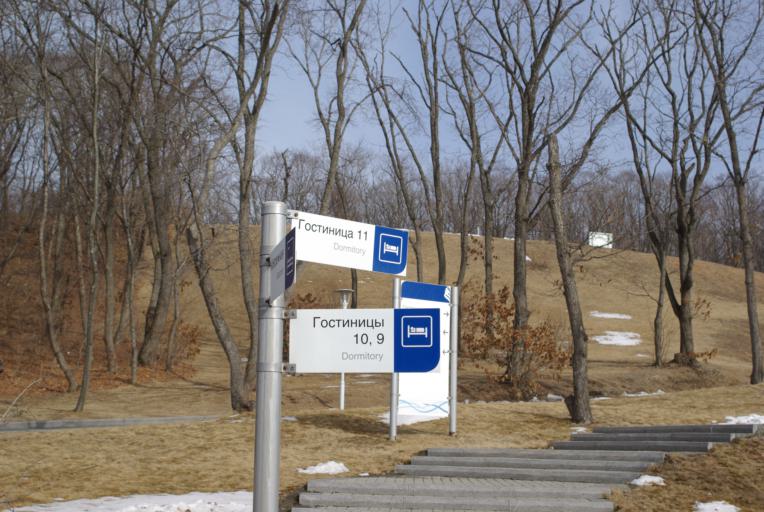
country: RU
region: Primorskiy
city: Russkiy
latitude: 43.0286
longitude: 131.9027
